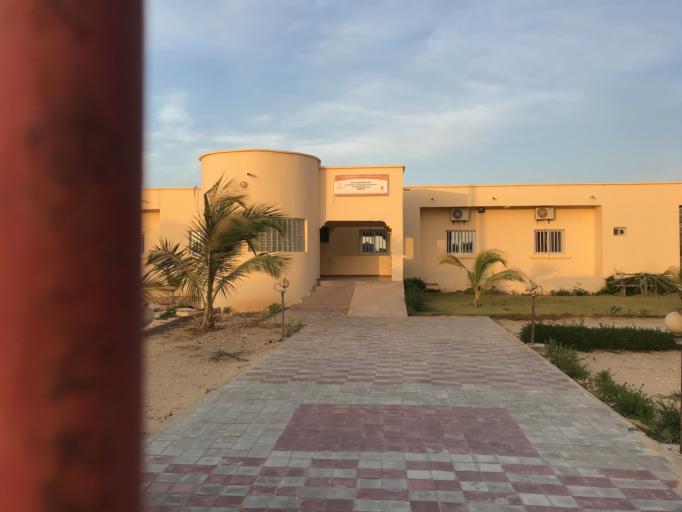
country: SN
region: Saint-Louis
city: Saint-Louis
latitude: 16.0492
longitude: -16.4335
